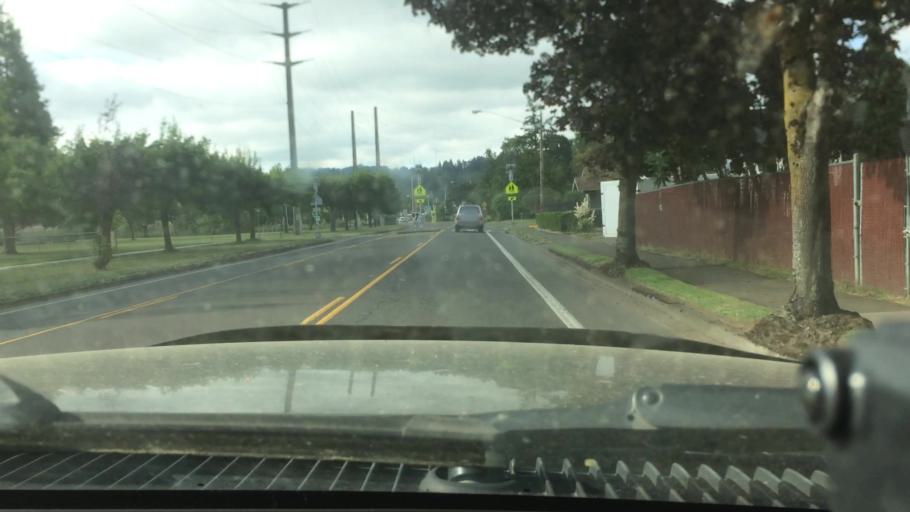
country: US
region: Oregon
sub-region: Lane County
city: Eugene
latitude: 44.0440
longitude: -123.1182
